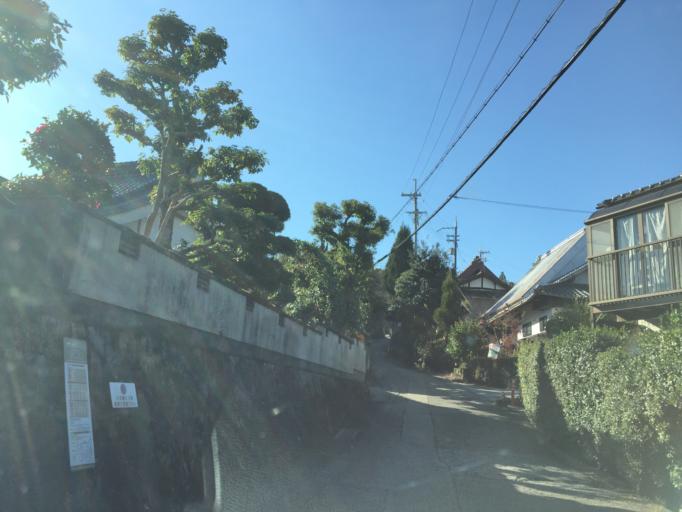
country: JP
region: Nara
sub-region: Ikoma-shi
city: Ikoma
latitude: 34.6673
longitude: 135.6951
